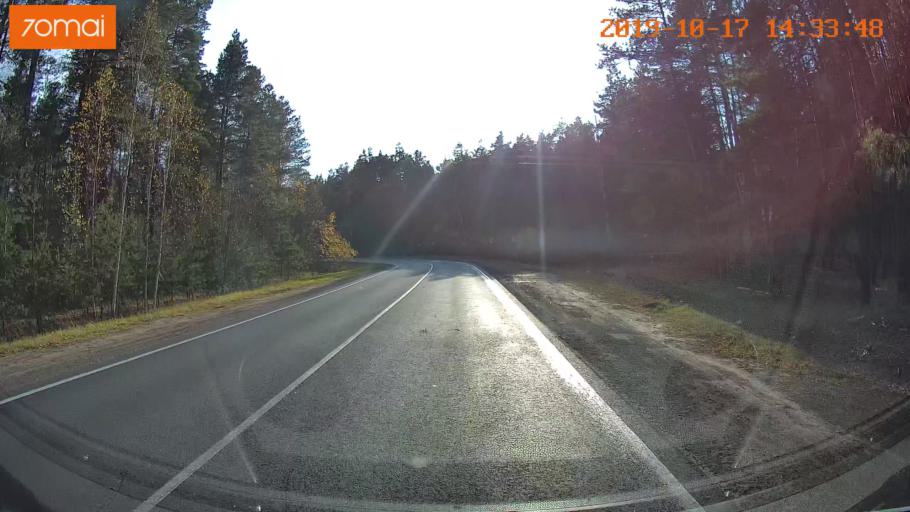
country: RU
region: Rjazan
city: Solotcha
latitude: 54.9196
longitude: 39.9968
